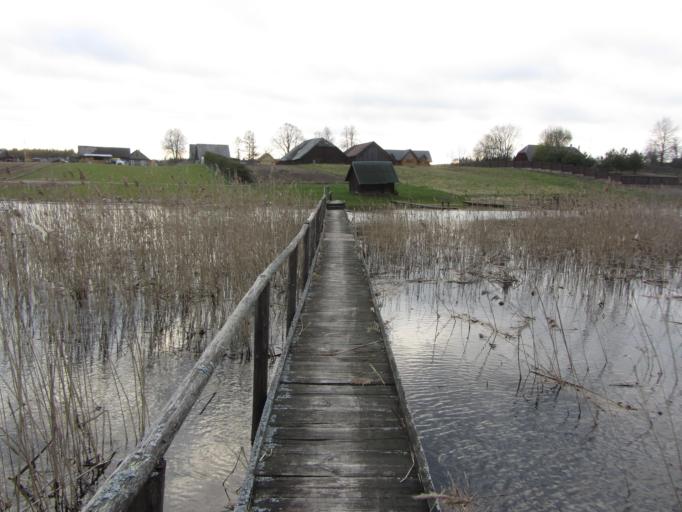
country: LT
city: Svencioneliai
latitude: 55.2620
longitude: 26.0038
